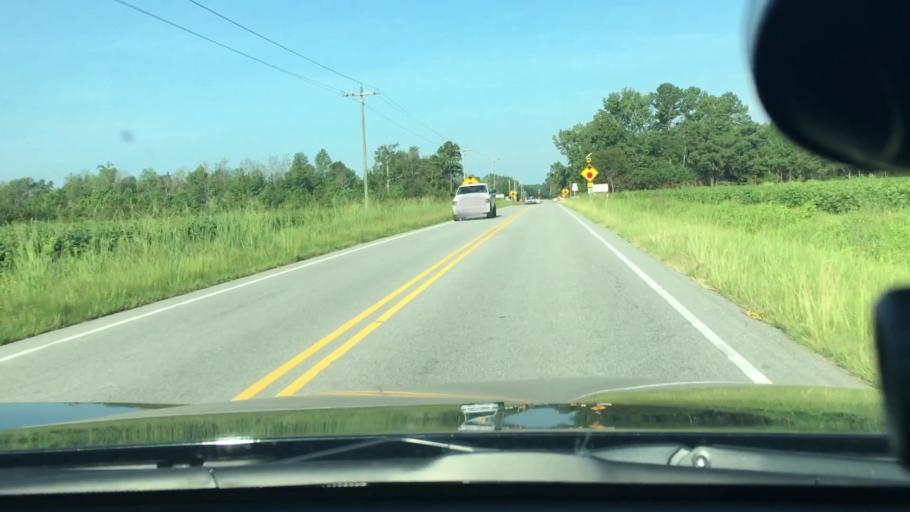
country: US
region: North Carolina
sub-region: Edgecombe County
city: Pinetops
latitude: 35.7808
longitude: -77.6006
